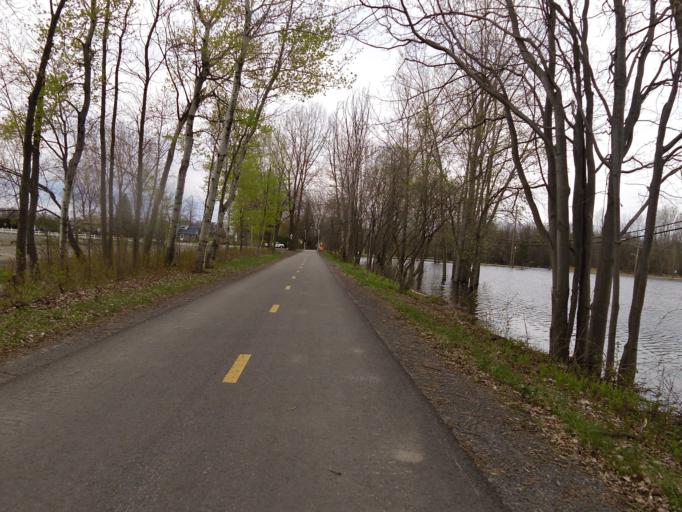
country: CA
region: Quebec
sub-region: Laurentides
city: Sainte-Marthe-sur-le-Lac
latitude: 45.5049
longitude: -73.9763
